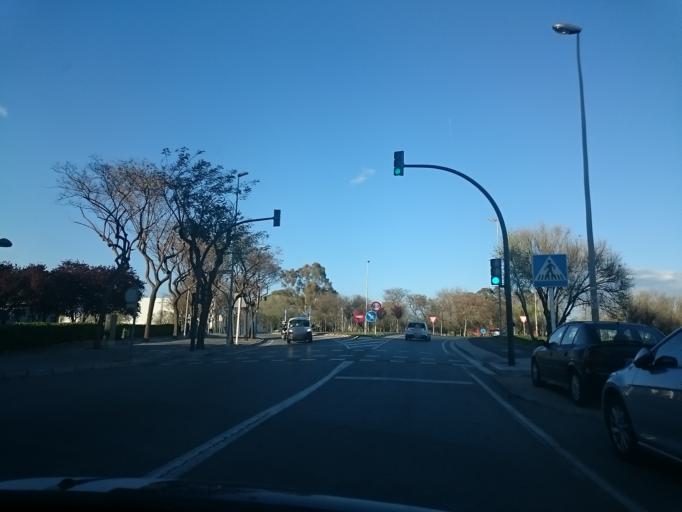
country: ES
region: Catalonia
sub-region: Provincia de Barcelona
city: El Prat de Llobregat
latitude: 41.3231
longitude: 2.1055
